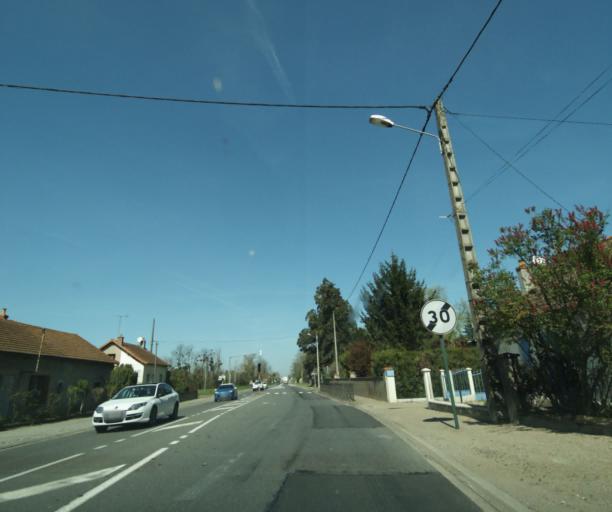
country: FR
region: Auvergne
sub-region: Departement de l'Allier
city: Trevol
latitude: 46.6617
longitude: 3.2460
